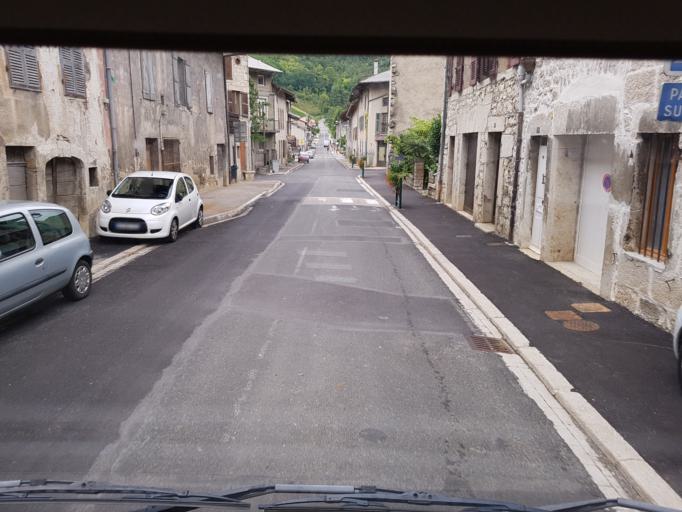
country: FR
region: Rhone-Alpes
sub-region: Departement de l'Ain
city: Poncin
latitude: 46.0810
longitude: 5.4660
